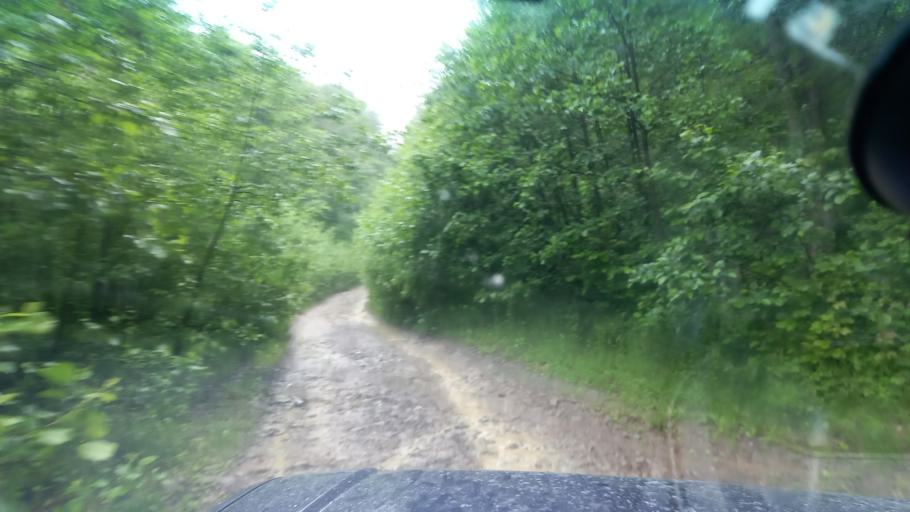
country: RU
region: Krasnodarskiy
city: Psebay
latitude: 43.9975
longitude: 40.6849
